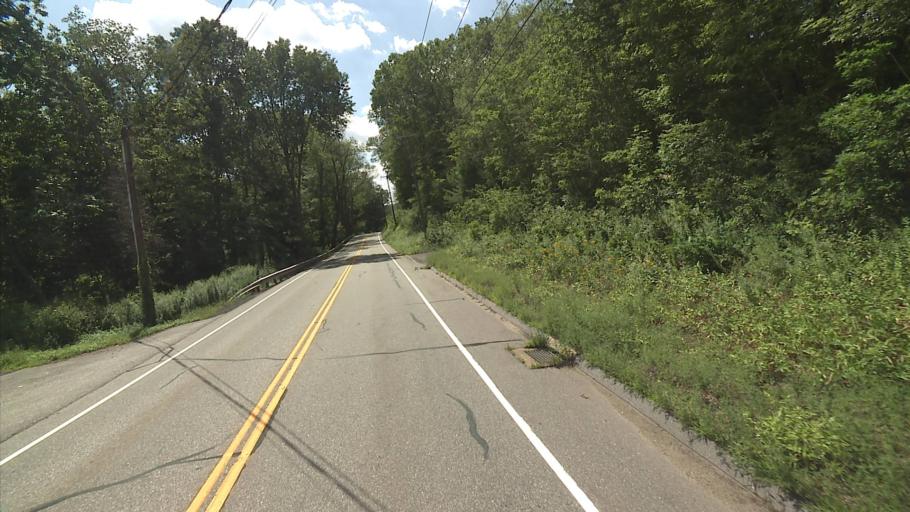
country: US
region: Connecticut
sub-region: Windham County
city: South Woodstock
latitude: 41.8958
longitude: -72.0790
